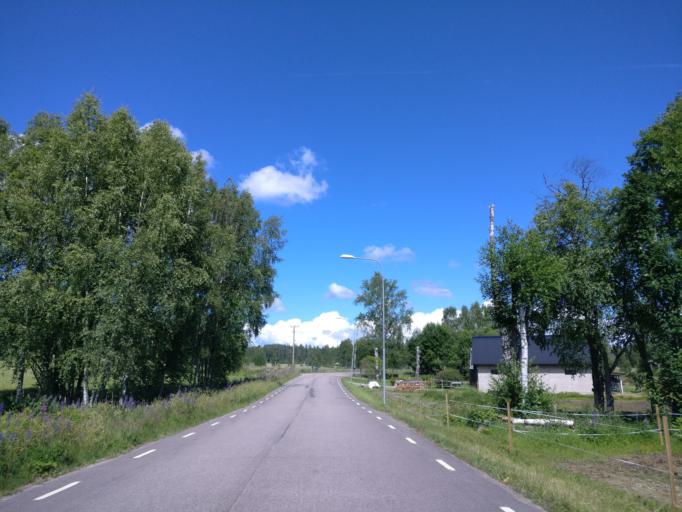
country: SE
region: Vaermland
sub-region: Hagfors Kommun
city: Hagfors
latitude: 60.0350
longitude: 13.6292
